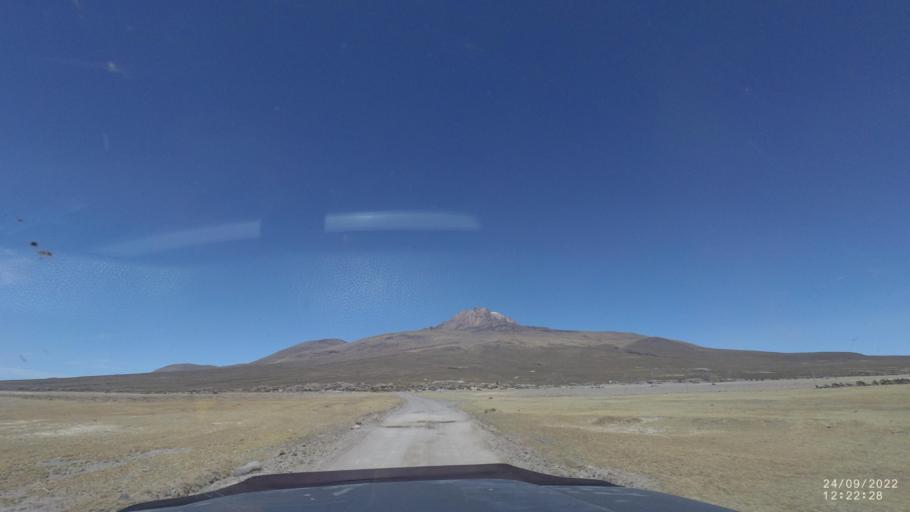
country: BO
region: Potosi
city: Colchani
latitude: -19.7566
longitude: -67.6651
